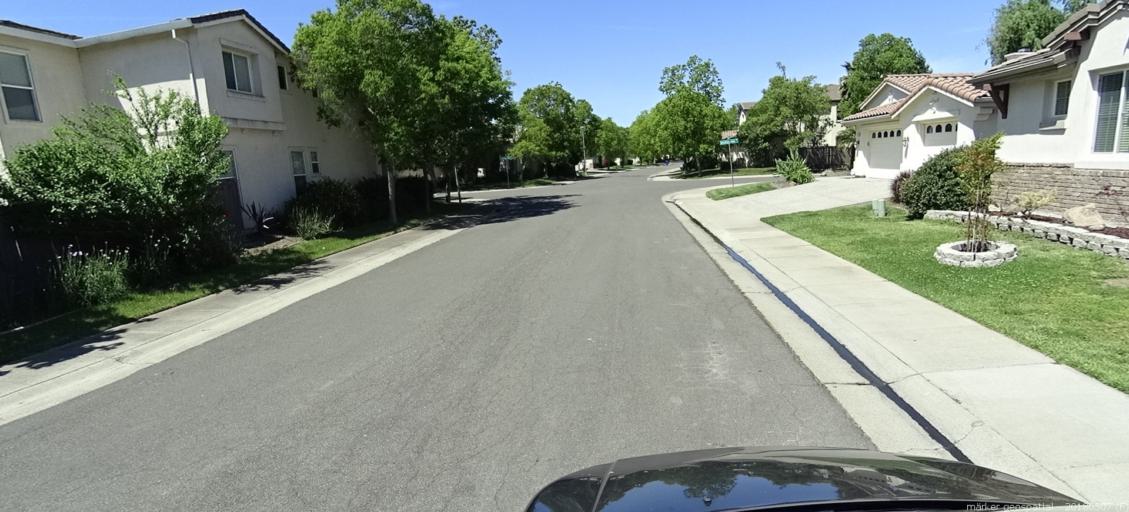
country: US
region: California
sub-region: Sacramento County
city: Rio Linda
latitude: 38.6683
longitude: -121.5087
